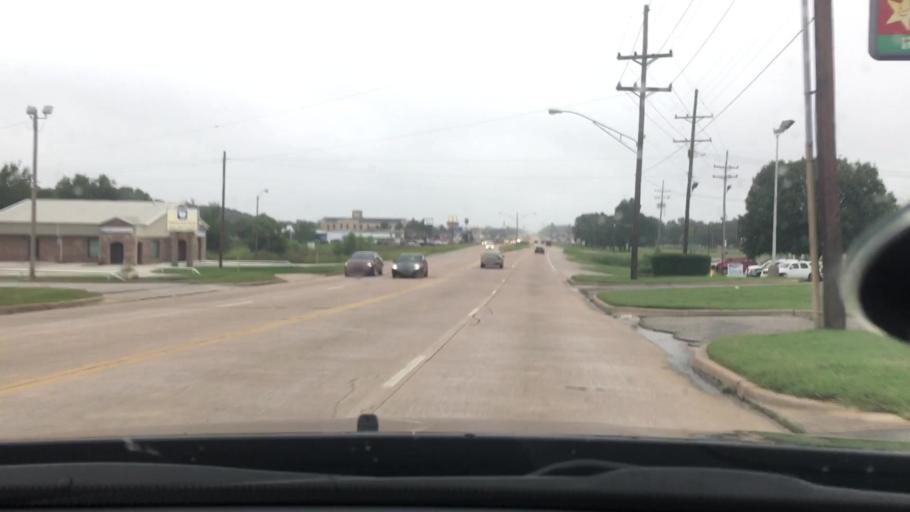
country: US
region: Oklahoma
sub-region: Seminole County
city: Seminole
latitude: 35.2335
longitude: -96.6710
